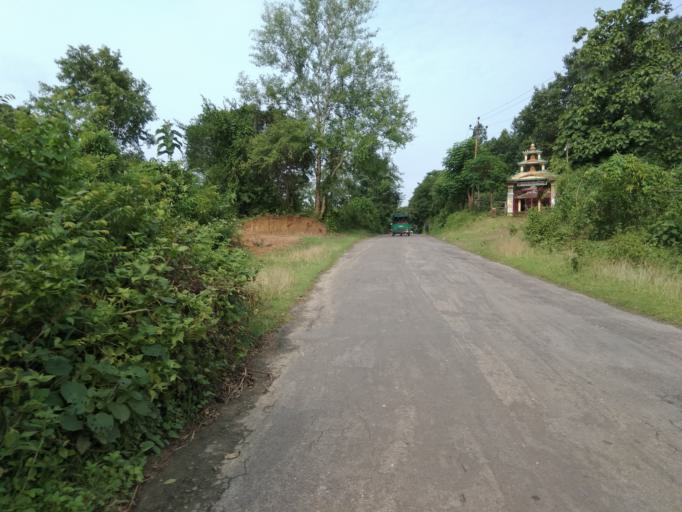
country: BD
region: Chittagong
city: Khagrachhari
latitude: 23.0113
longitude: 92.0130
